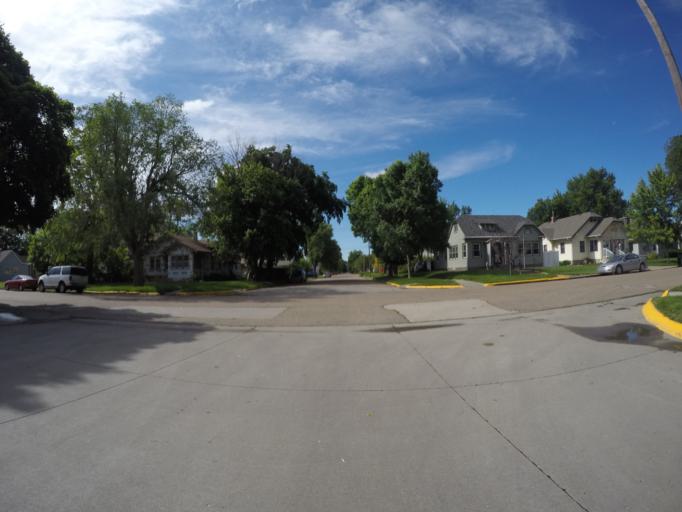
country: US
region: Nebraska
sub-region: Buffalo County
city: Kearney
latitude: 40.7027
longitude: -99.0898
